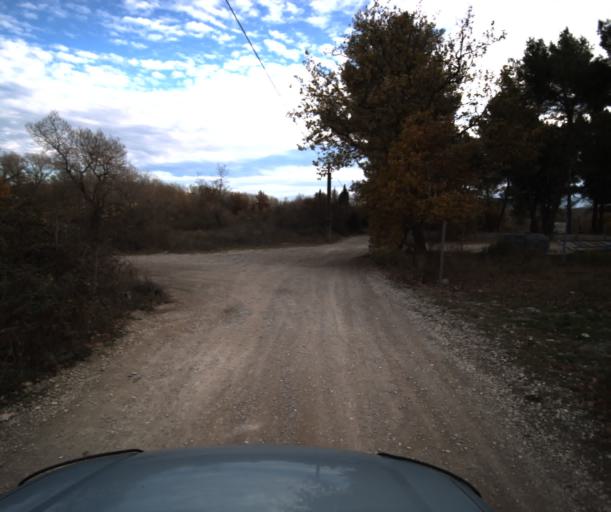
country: FR
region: Provence-Alpes-Cote d'Azur
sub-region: Departement des Bouches-du-Rhone
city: Meyrargues
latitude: 43.6632
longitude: 5.5303
